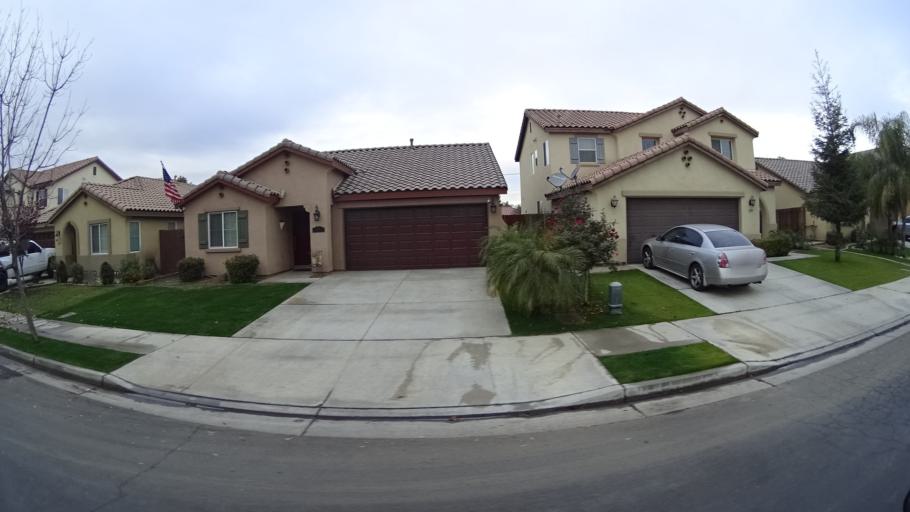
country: US
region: California
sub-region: Kern County
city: Greenfield
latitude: 35.2992
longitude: -119.0738
